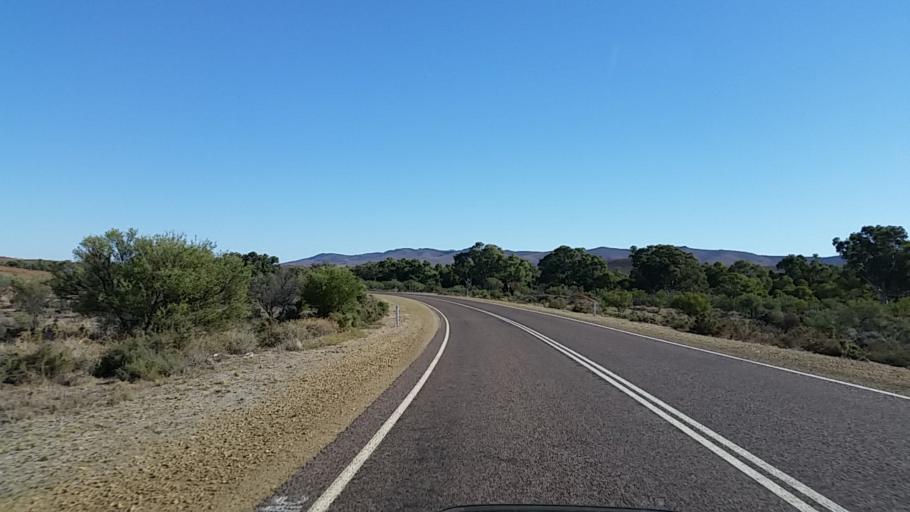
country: AU
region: South Australia
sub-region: Flinders Ranges
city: Quorn
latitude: -32.3284
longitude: 138.4756
